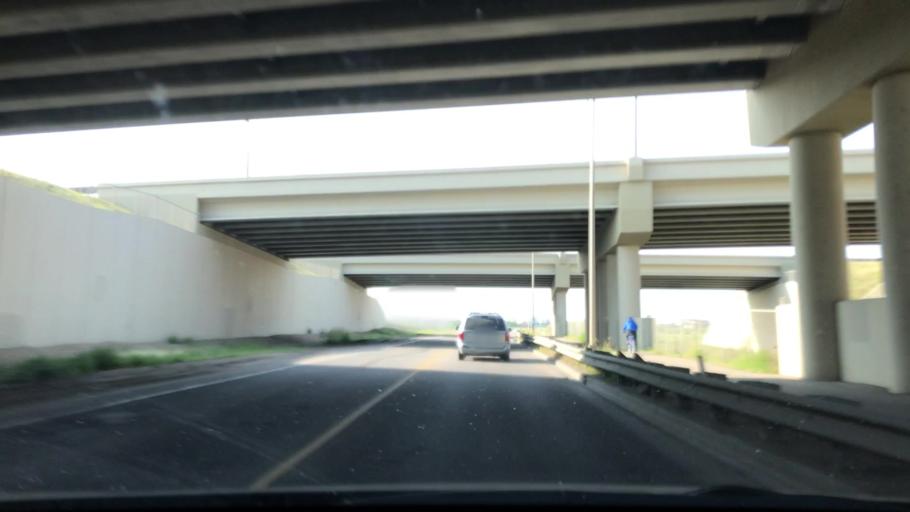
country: CA
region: Alberta
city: Beaumont
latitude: 53.4379
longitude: -113.4837
